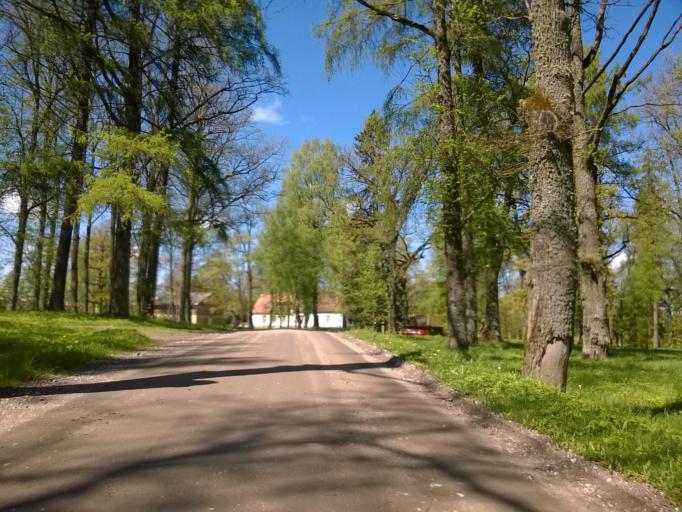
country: LV
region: Amatas Novads
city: Drabesi
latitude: 57.2428
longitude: 25.2817
